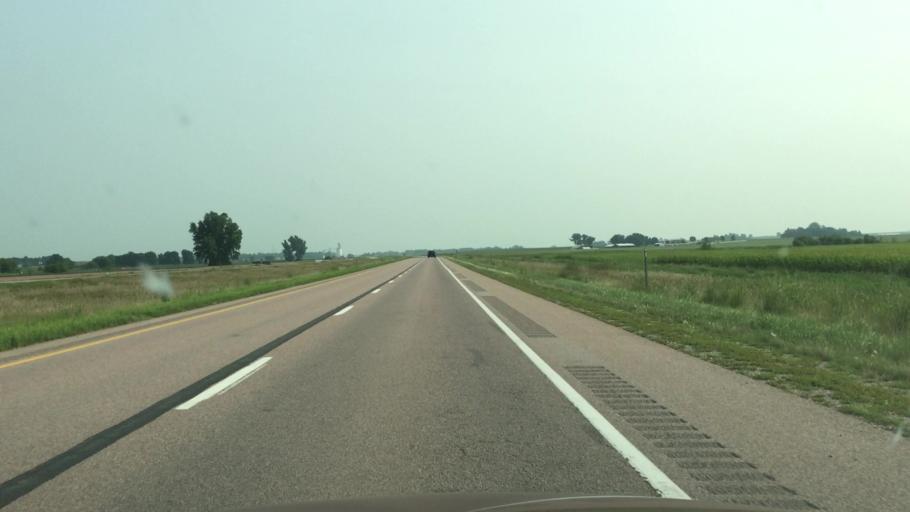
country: US
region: Iowa
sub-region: O'Brien County
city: Sheldon
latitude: 43.2774
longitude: -95.8029
